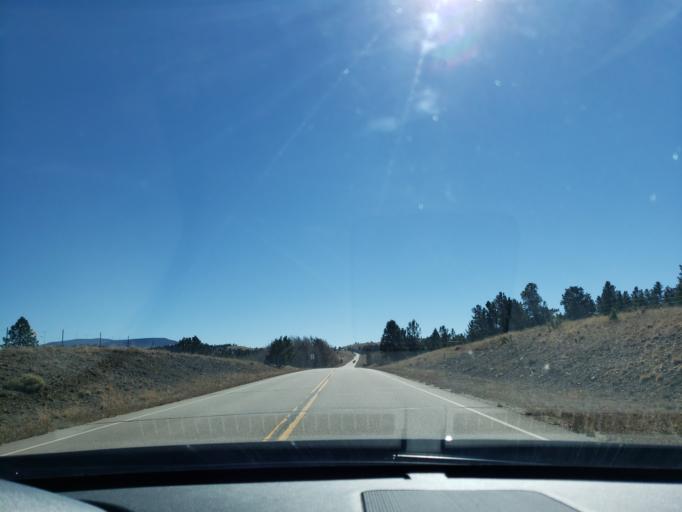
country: US
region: Colorado
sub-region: Chaffee County
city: Buena Vista
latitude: 38.9076
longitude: -105.6994
